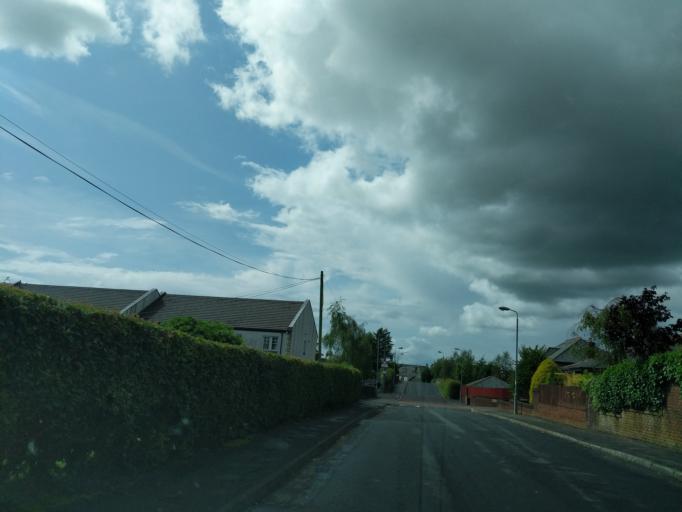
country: GB
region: Scotland
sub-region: East Ayrshire
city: Stewarton
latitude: 55.7123
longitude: -4.5305
